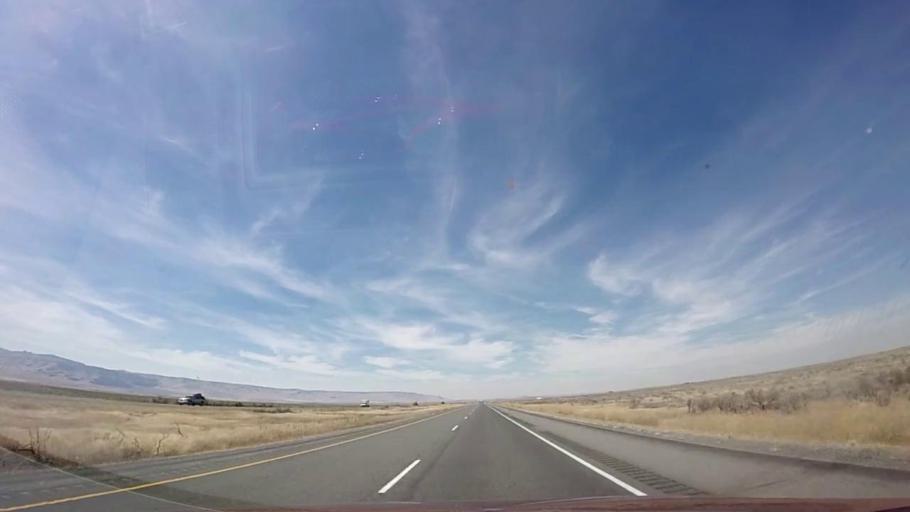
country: US
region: Idaho
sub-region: Minidoka County
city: Rupert
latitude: 42.3748
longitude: -113.2716
